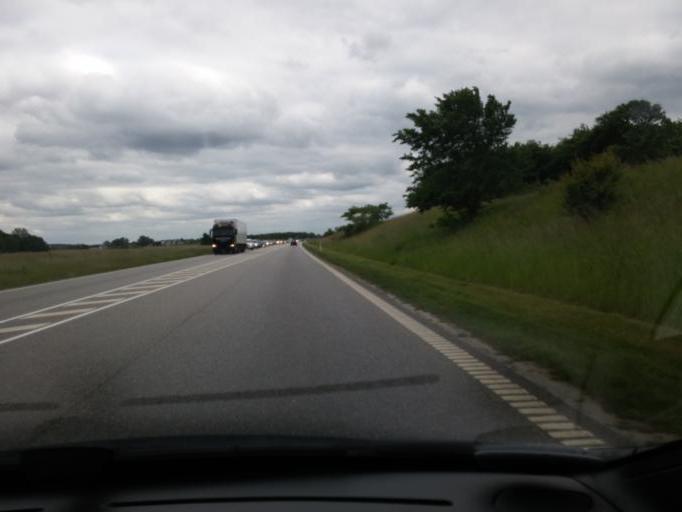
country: DK
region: Capital Region
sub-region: Allerod Kommune
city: Lillerod
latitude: 55.8768
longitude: 12.3077
